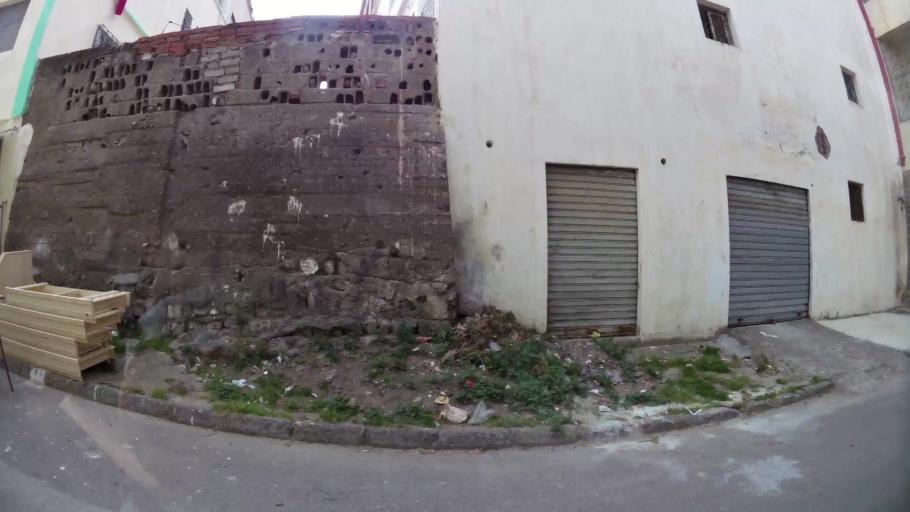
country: MA
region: Tanger-Tetouan
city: Tetouan
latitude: 35.5814
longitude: -5.3555
